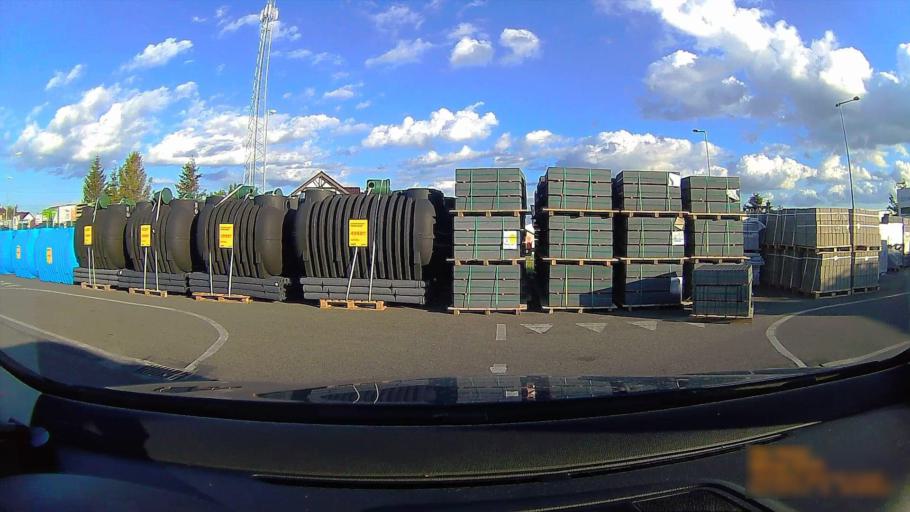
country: PL
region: Greater Poland Voivodeship
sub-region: Kalisz
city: Kalisz
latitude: 51.7373
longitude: 18.0433
